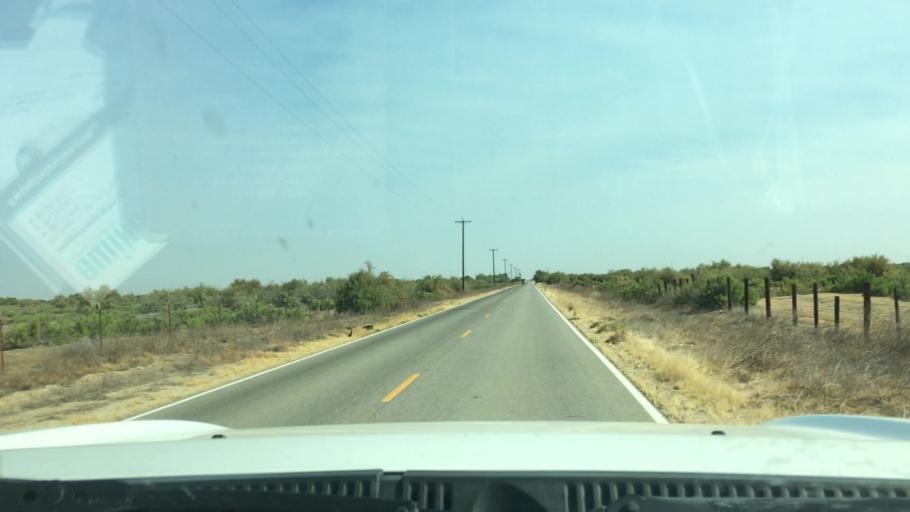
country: US
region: California
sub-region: Kern County
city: Lost Hills
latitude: 35.7094
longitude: -119.5796
